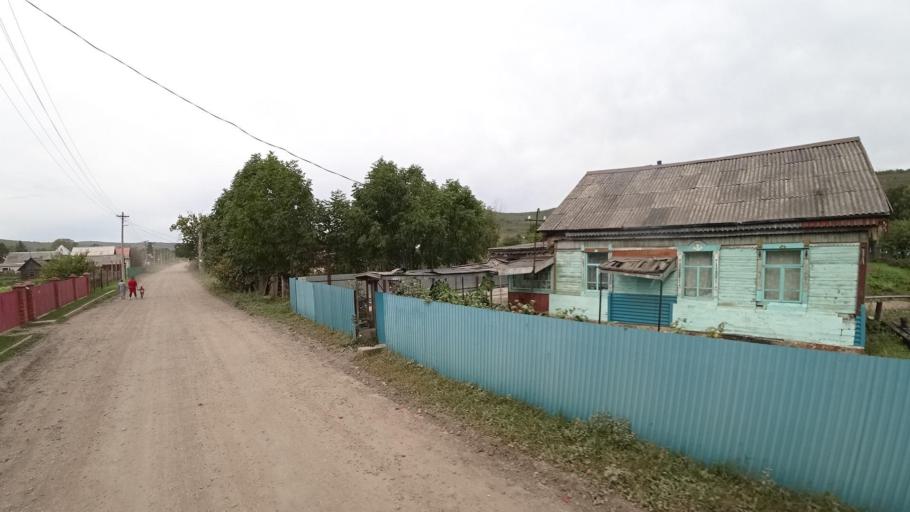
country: RU
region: Jewish Autonomous Oblast
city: Khingansk
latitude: 49.0327
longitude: 131.0492
